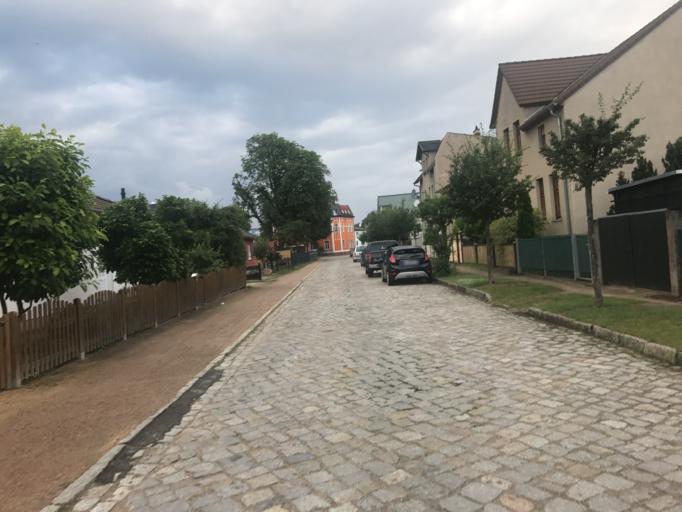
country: DE
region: Brandenburg
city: Melchow
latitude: 52.8407
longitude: 13.6887
